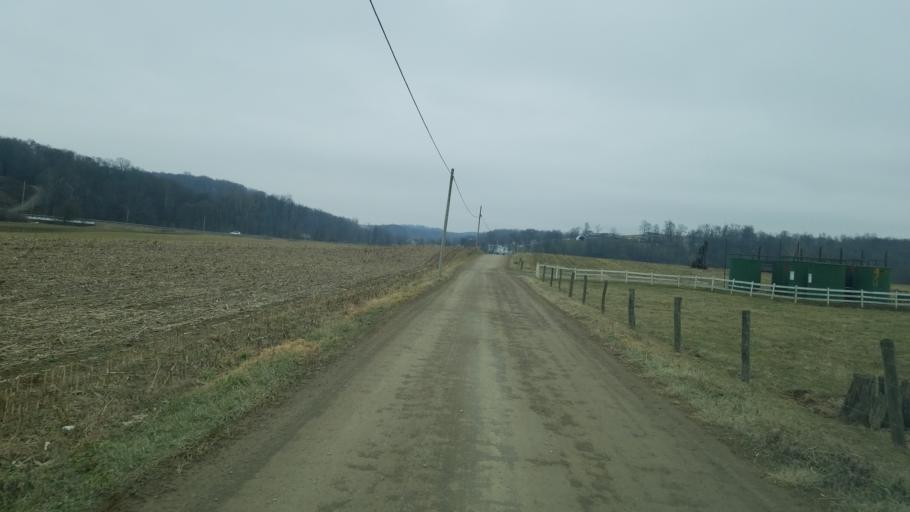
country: US
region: Ohio
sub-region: Holmes County
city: Millersburg
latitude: 40.4692
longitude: -81.8561
